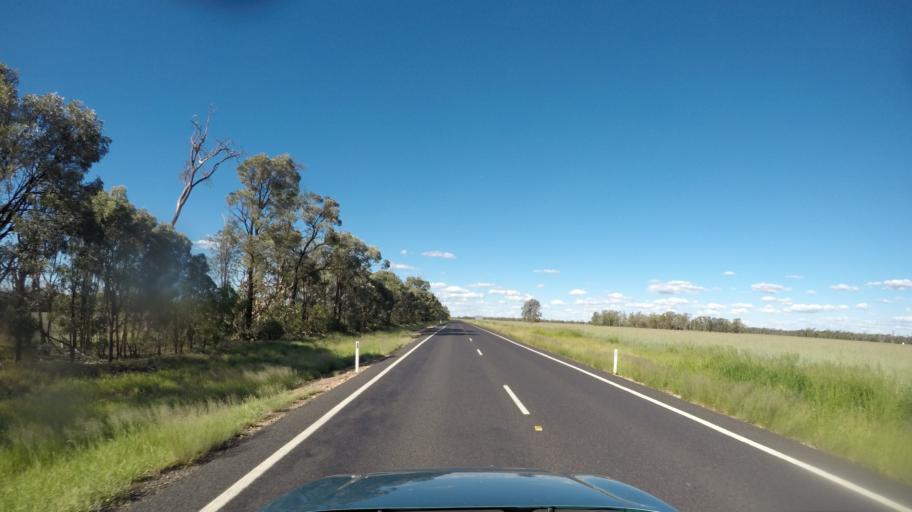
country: AU
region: Queensland
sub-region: Goondiwindi
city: Goondiwindi
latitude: -28.1330
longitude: 150.6981
